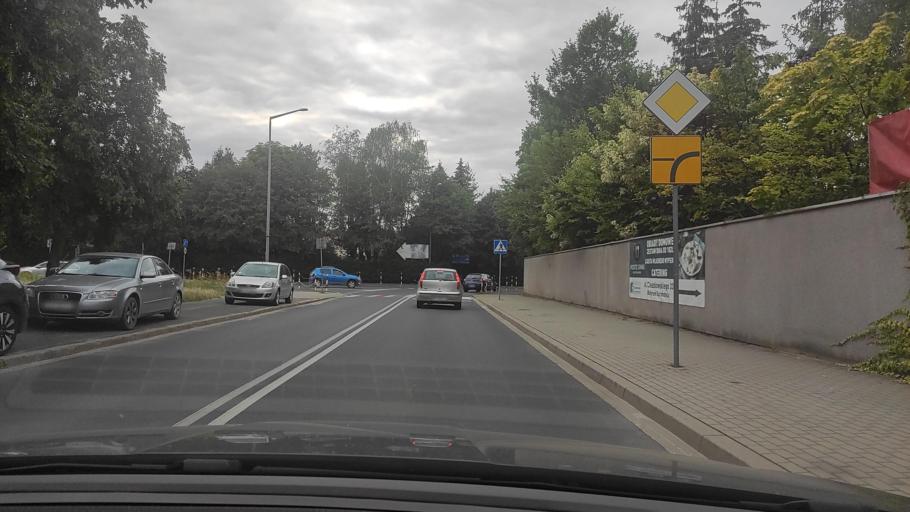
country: PL
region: Greater Poland Voivodeship
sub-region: Powiat poznanski
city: Swarzedz
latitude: 52.4157
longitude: 17.0844
